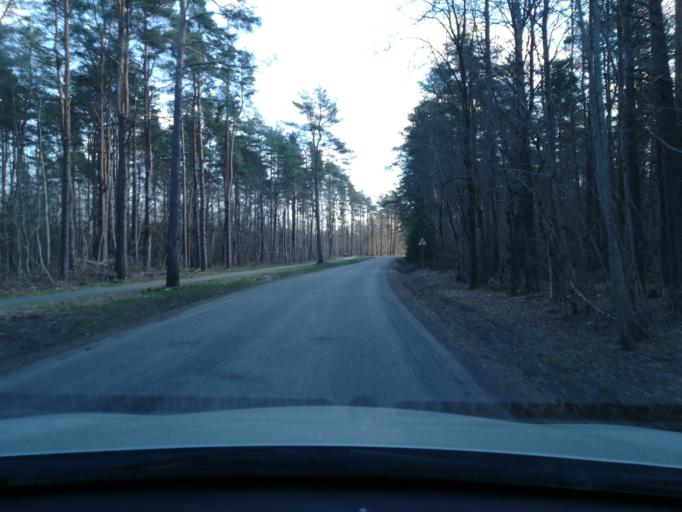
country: EE
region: Harju
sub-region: Saue vald
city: Laagri
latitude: 59.3546
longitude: 24.5837
